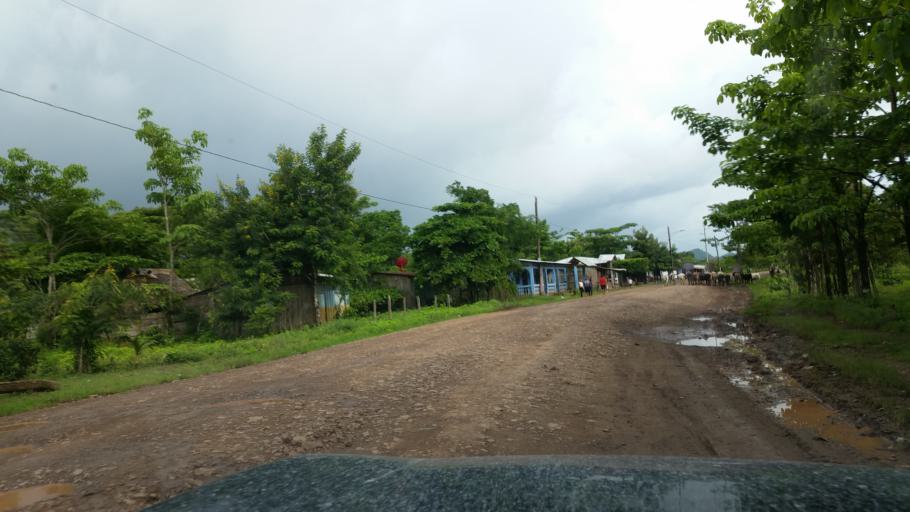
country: NI
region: Atlantico Norte (RAAN)
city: Siuna
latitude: 13.4312
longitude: -84.8528
